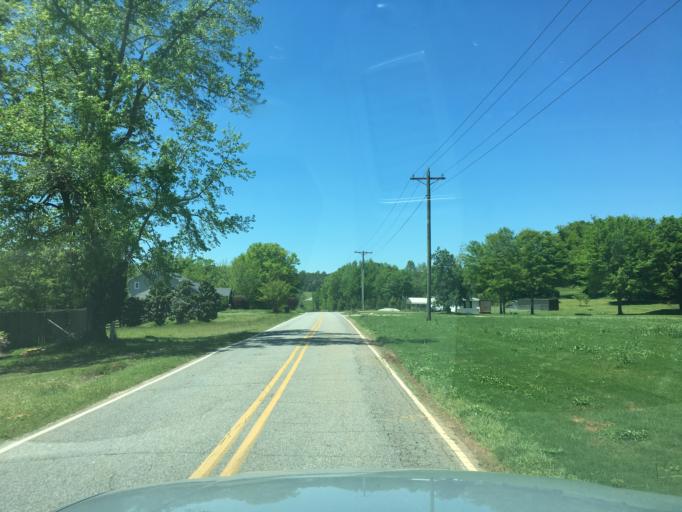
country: US
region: South Carolina
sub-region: Greenville County
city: Five Forks
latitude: 34.8560
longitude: -82.1635
